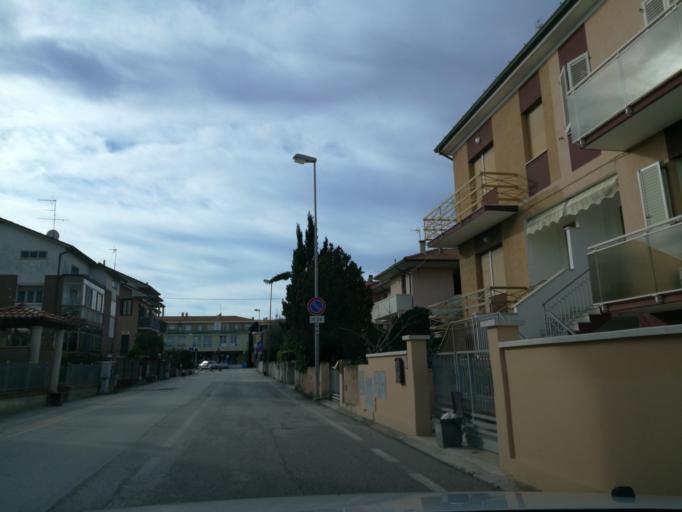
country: IT
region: The Marches
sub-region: Provincia di Pesaro e Urbino
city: Marotta
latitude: 43.7748
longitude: 13.1252
